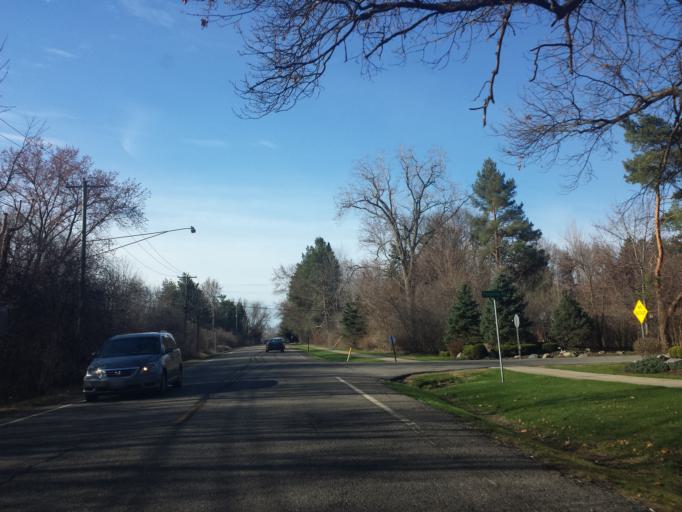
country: US
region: Michigan
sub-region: Oakland County
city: Franklin
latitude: 42.5376
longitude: -83.3028
